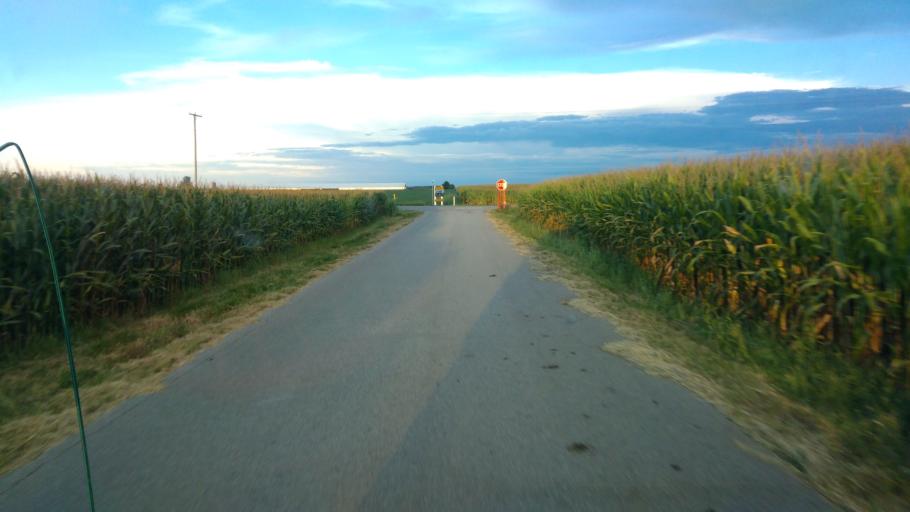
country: US
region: Ohio
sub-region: Crawford County
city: Bucyrus
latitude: 40.7321
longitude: -82.9970
